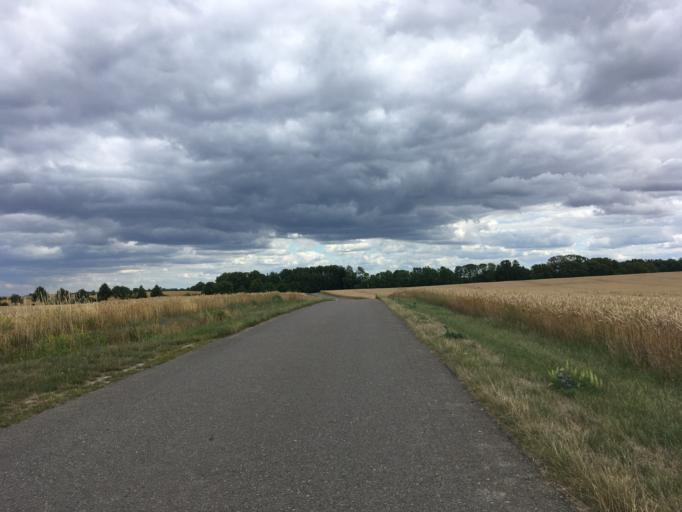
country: DE
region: Brandenburg
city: Gramzow
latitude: 53.2533
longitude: 13.9929
